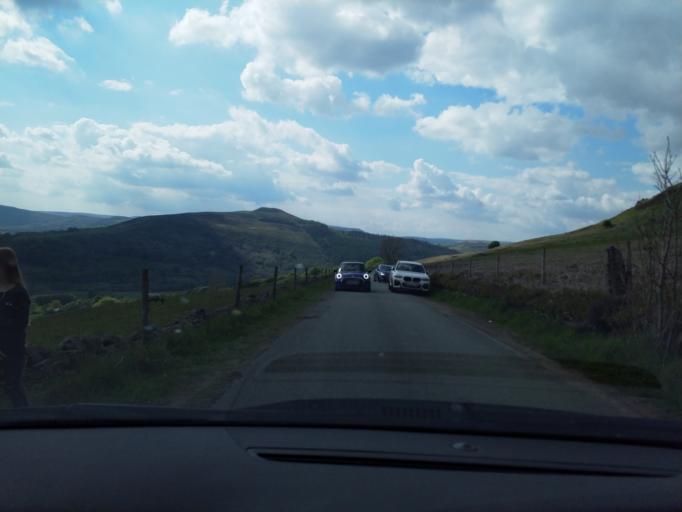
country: GB
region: England
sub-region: Derbyshire
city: Hathersage
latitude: 53.3530
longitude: -1.6822
